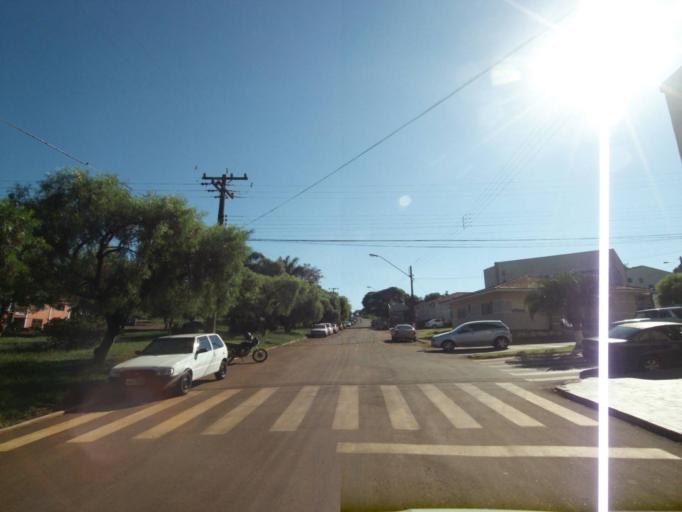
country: BR
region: Parana
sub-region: Laranjeiras Do Sul
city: Laranjeiras do Sul
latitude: -25.4887
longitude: -52.5270
